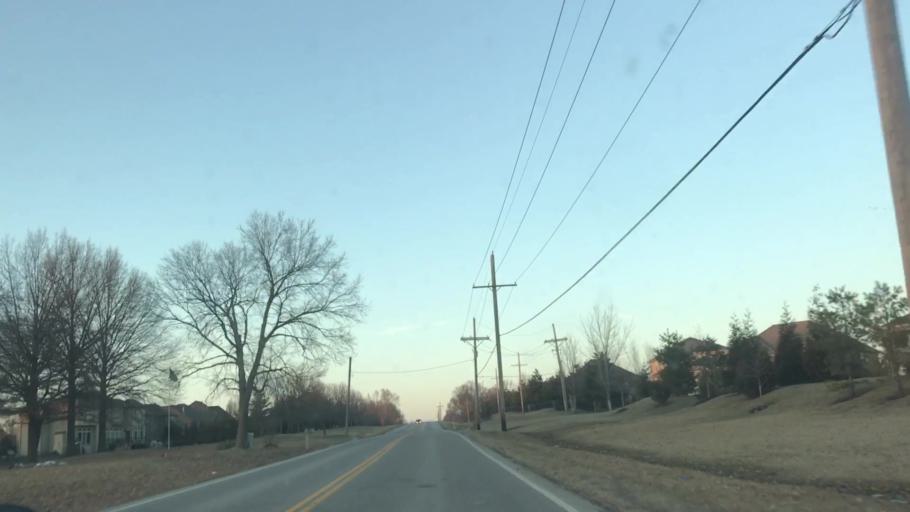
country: US
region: Kansas
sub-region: Johnson County
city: Olathe
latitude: 38.8320
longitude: -94.7052
